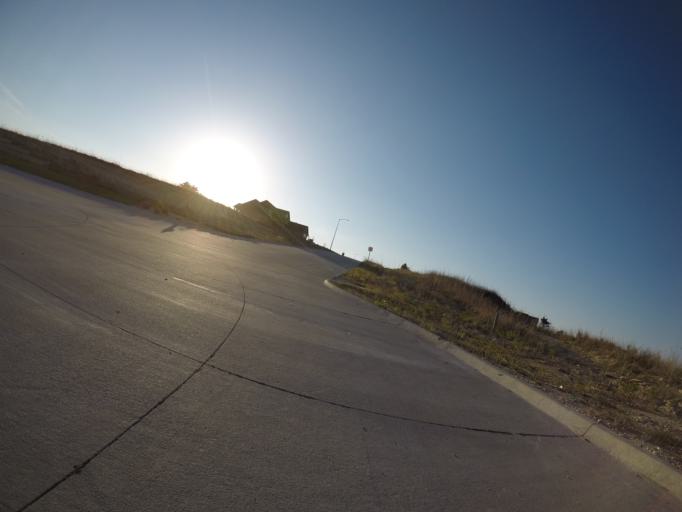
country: US
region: Kansas
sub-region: Riley County
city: Manhattan
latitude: 39.2098
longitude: -96.6367
